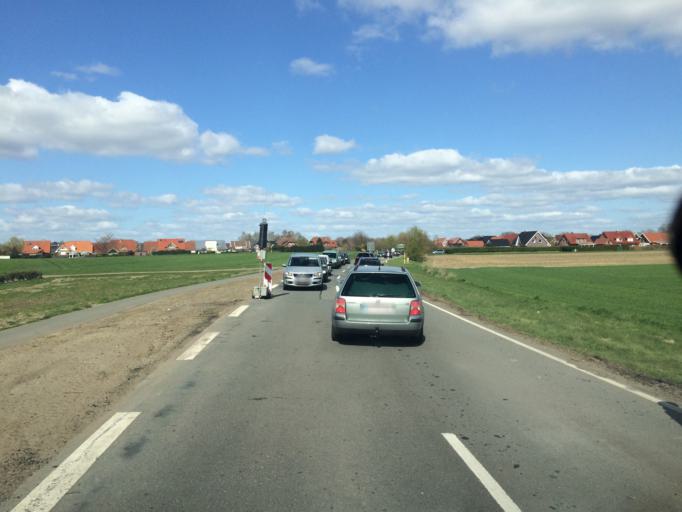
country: DE
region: Lower Saxony
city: Haren
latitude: 52.7810
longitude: 7.2203
